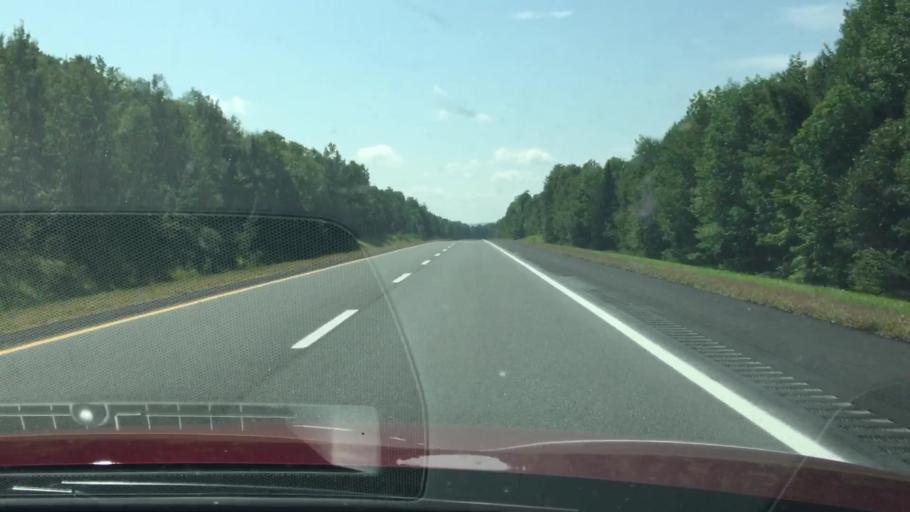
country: US
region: Maine
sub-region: Penobscot County
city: Patten
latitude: 45.9432
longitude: -68.3443
